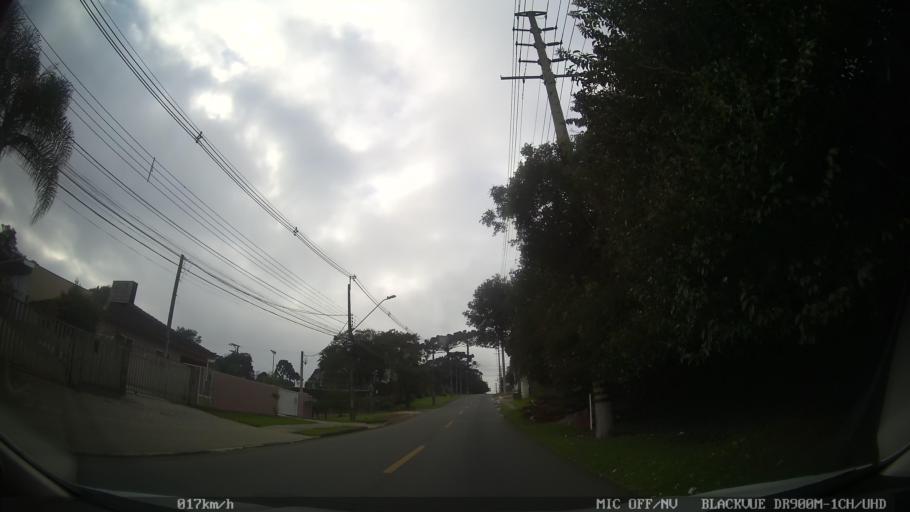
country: BR
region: Parana
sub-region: Curitiba
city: Curitiba
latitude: -25.3936
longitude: -49.3229
